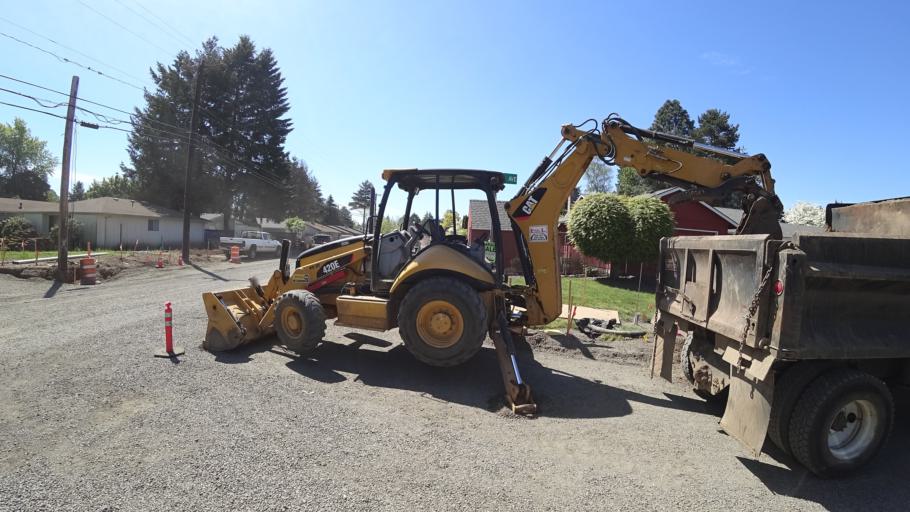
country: US
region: Oregon
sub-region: Washington County
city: Hillsboro
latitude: 45.5162
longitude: -122.9467
